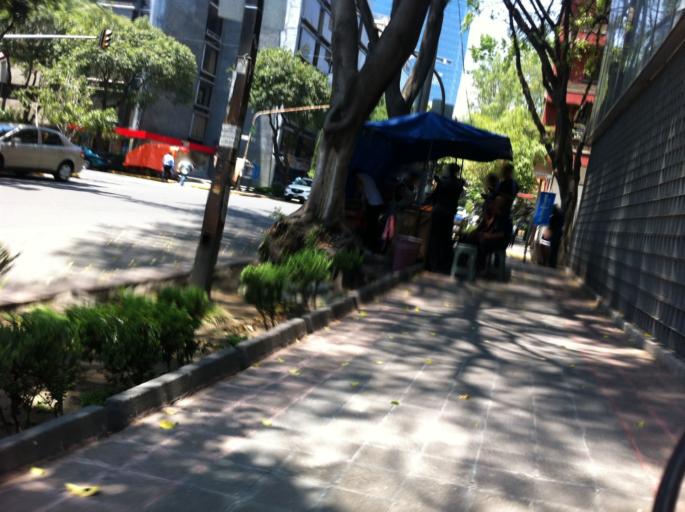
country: MX
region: Mexico City
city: Cuauhtemoc
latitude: 19.4269
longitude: -99.1580
